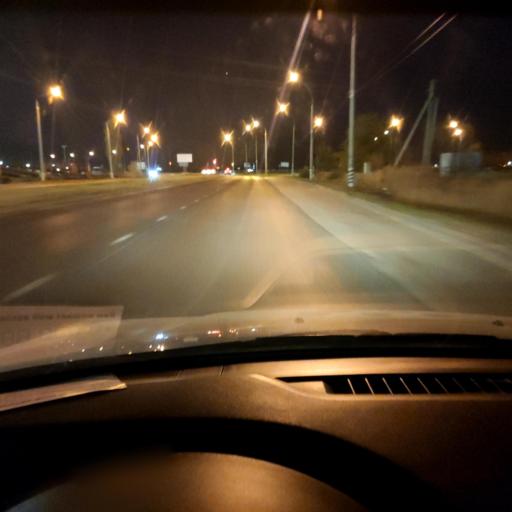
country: RU
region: Samara
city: Tol'yatti
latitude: 53.5563
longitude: 49.3441
